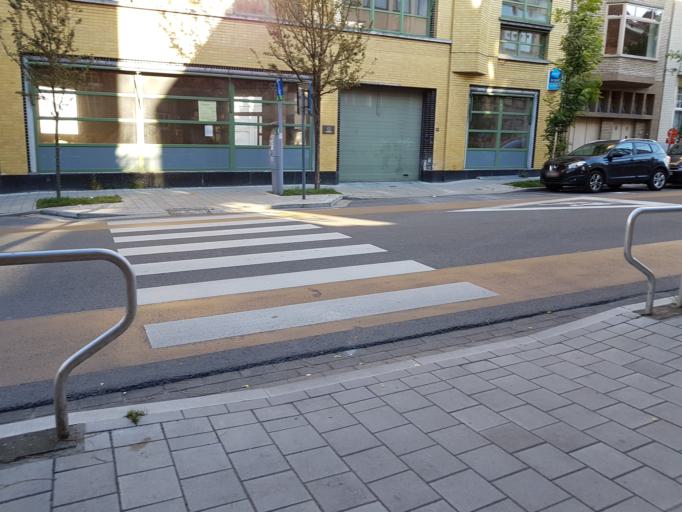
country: BE
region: Flanders
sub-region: Provincie Oost-Vlaanderen
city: Ledeberg
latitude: 51.0416
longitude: 3.7329
